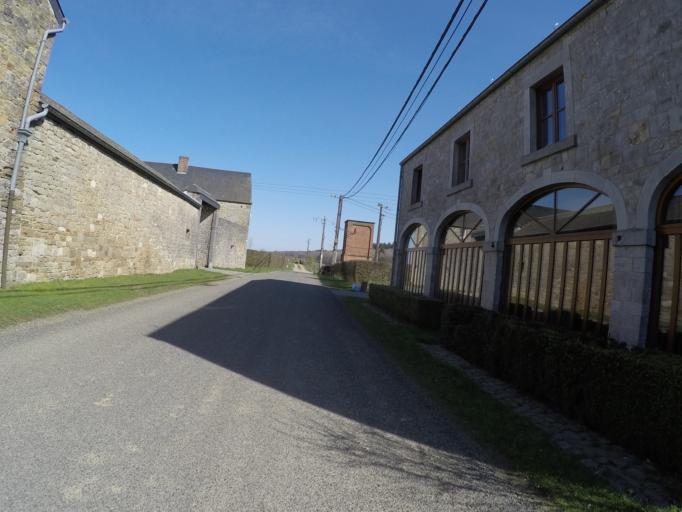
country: BE
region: Wallonia
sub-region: Province de Namur
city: Gesves
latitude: 50.3596
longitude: 5.0844
